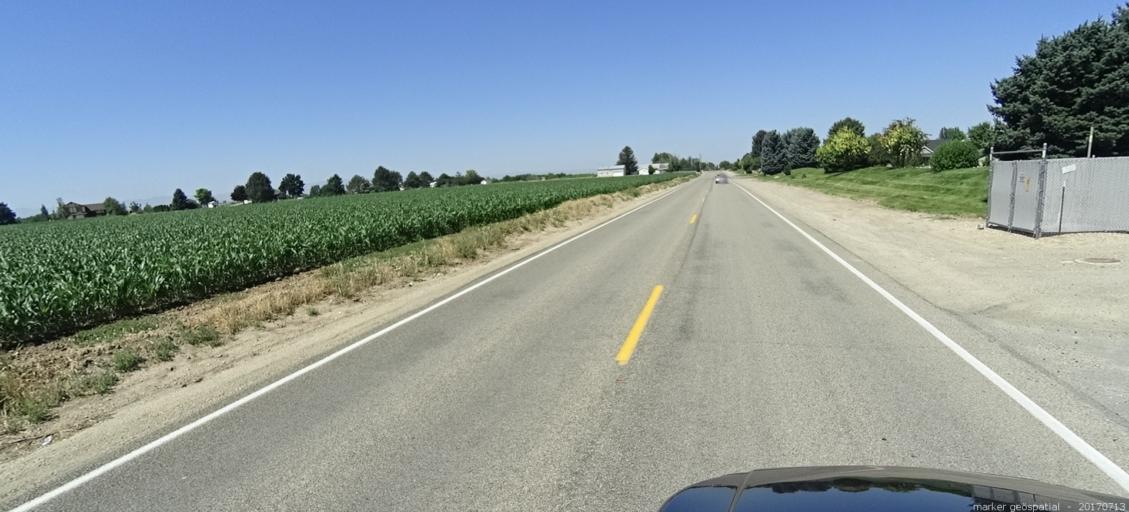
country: US
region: Idaho
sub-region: Ada County
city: Kuna
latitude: 43.5321
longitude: -116.4455
